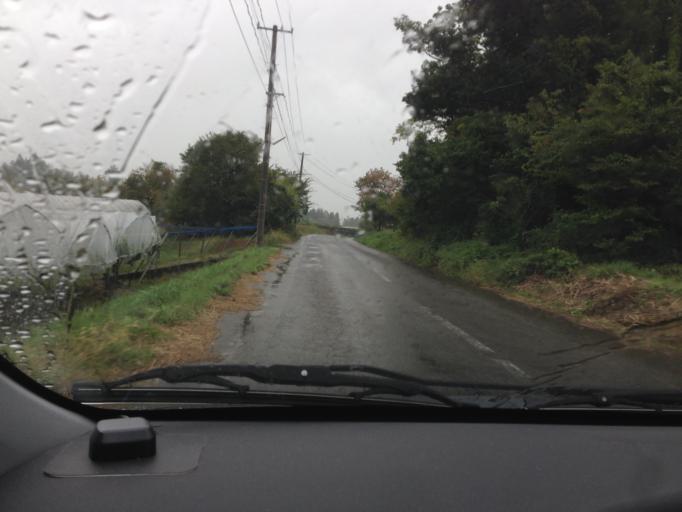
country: JP
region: Fukushima
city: Kitakata
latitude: 37.5061
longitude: 139.8158
